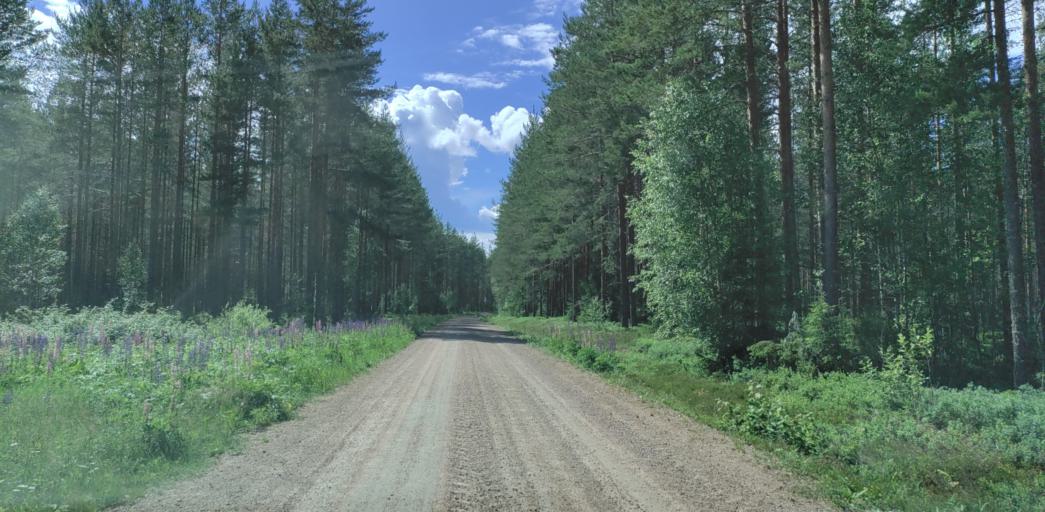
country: SE
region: Vaermland
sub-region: Munkfors Kommun
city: Munkfors
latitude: 59.9602
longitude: 13.5017
